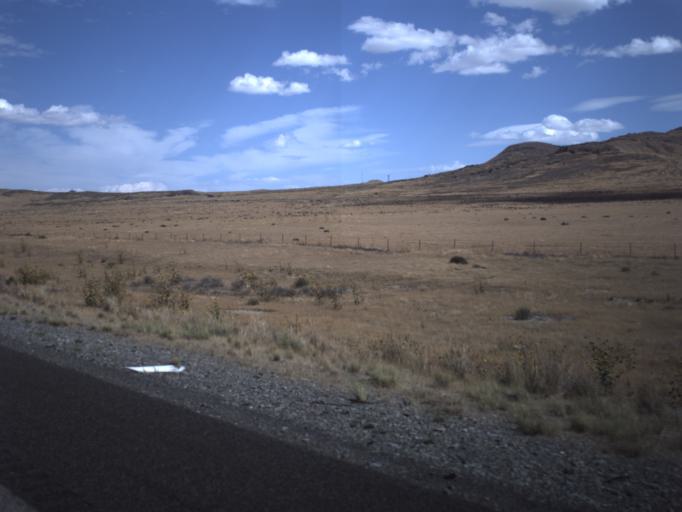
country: US
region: Utah
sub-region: Tooele County
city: Grantsville
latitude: 40.7951
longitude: -112.9493
